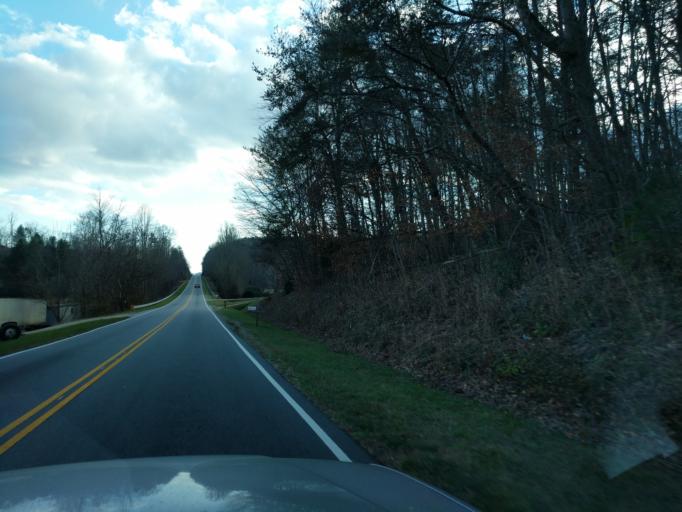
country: US
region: North Carolina
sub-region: McDowell County
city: West Marion
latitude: 35.6096
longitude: -81.9851
